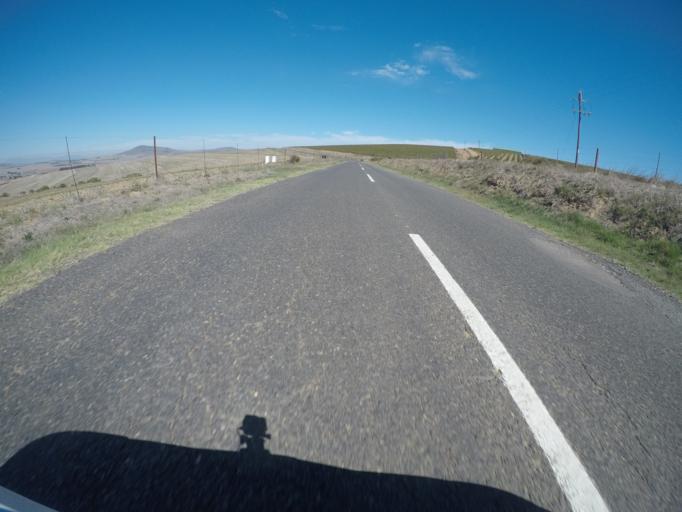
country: ZA
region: Western Cape
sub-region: City of Cape Town
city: Sunset Beach
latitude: -33.7111
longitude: 18.5825
